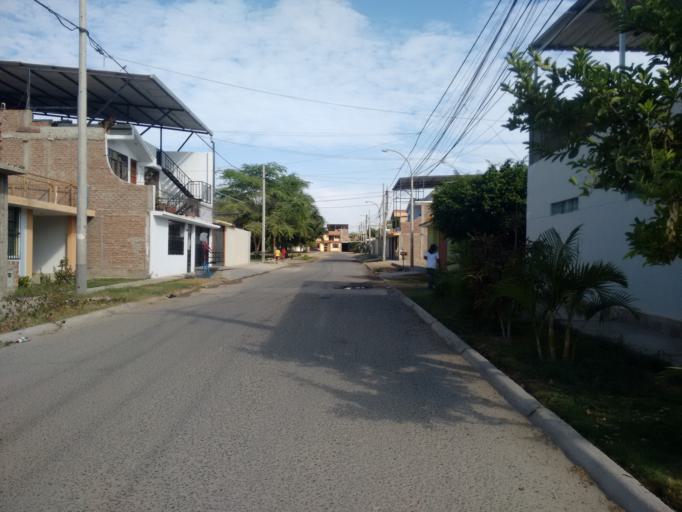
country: PE
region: Piura
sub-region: Provincia de Piura
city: Piura
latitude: -5.1735
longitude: -80.6429
